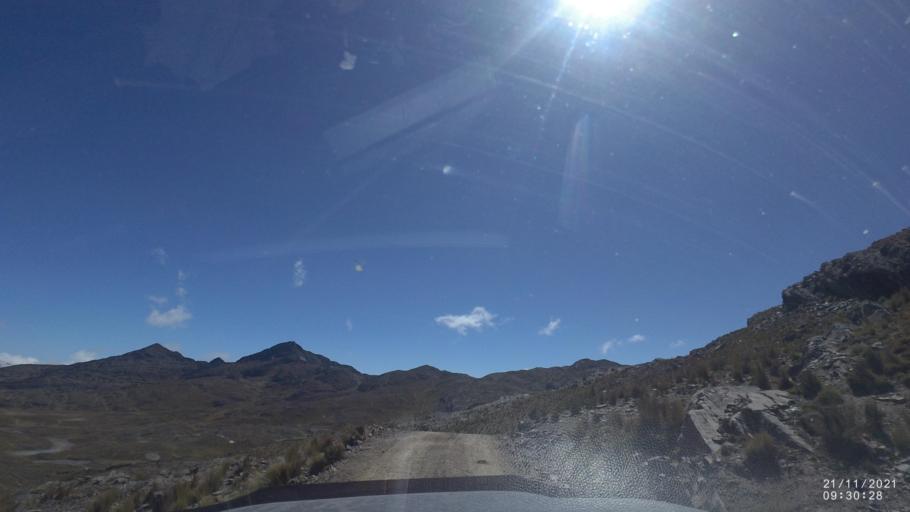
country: BO
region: Cochabamba
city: Cochabamba
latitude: -17.0759
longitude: -66.2564
